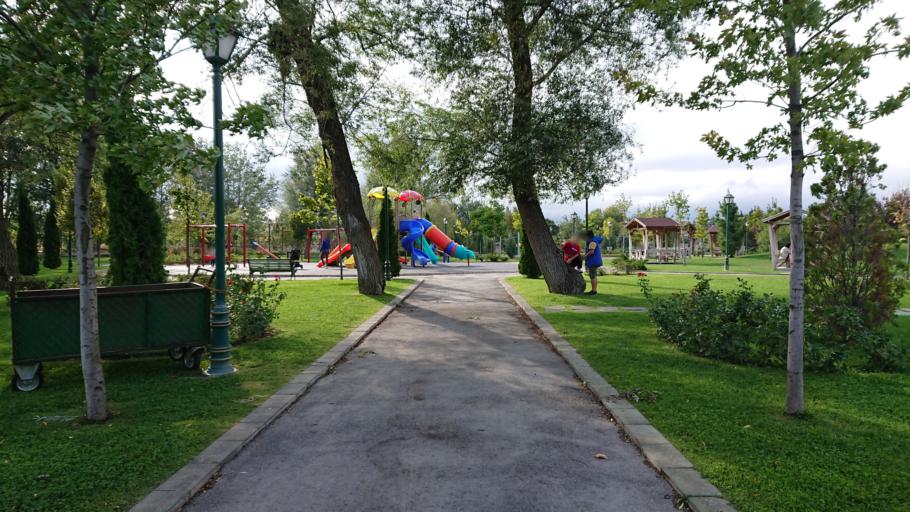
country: TR
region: Eskisehir
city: Eskisehir
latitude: 39.7620
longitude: 30.4870
